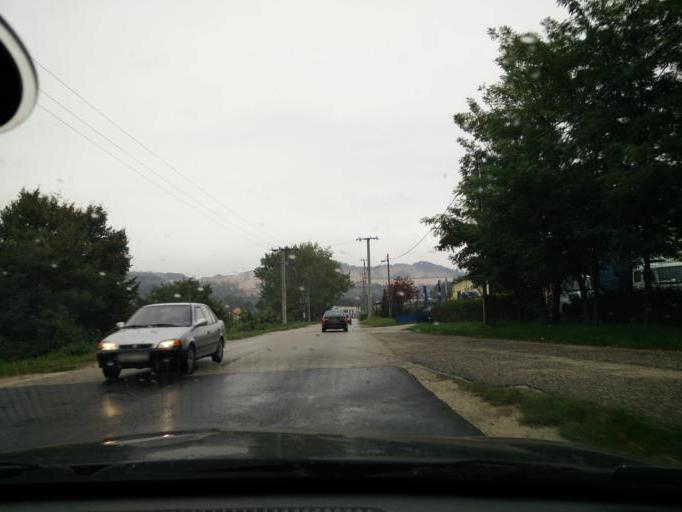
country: HU
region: Komarom-Esztergom
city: Tatabanya
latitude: 47.5634
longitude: 18.4375
